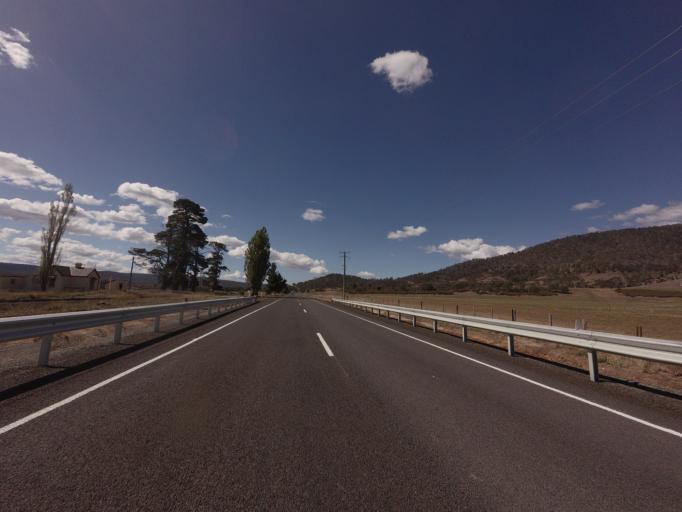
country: AU
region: Tasmania
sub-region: Break O'Day
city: St Helens
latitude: -41.6693
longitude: 147.9033
